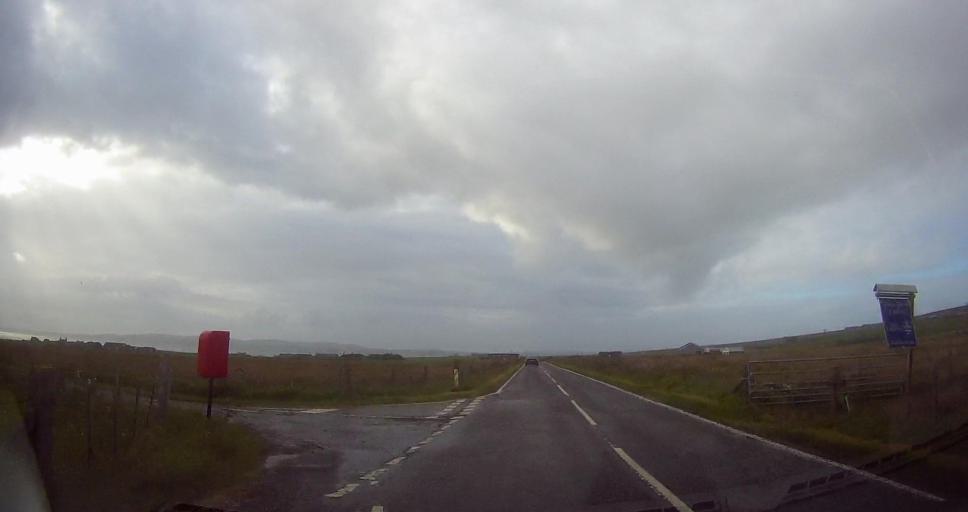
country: GB
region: Scotland
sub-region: Orkney Islands
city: Stromness
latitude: 58.9337
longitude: -3.2098
